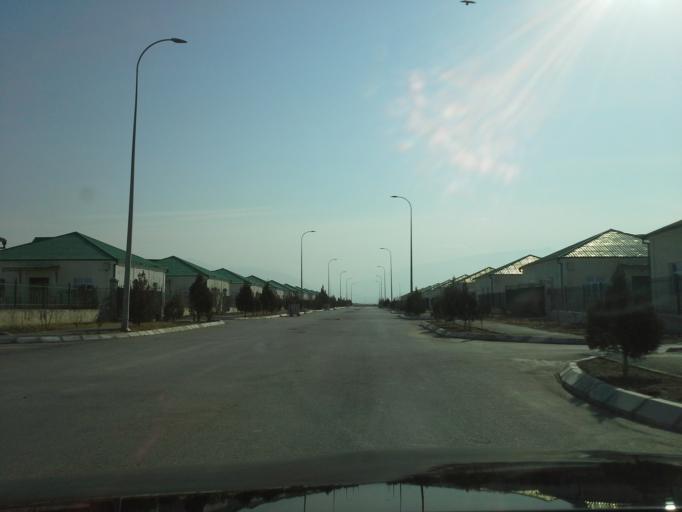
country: TM
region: Ahal
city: Abadan
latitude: 38.1673
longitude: 58.0508
